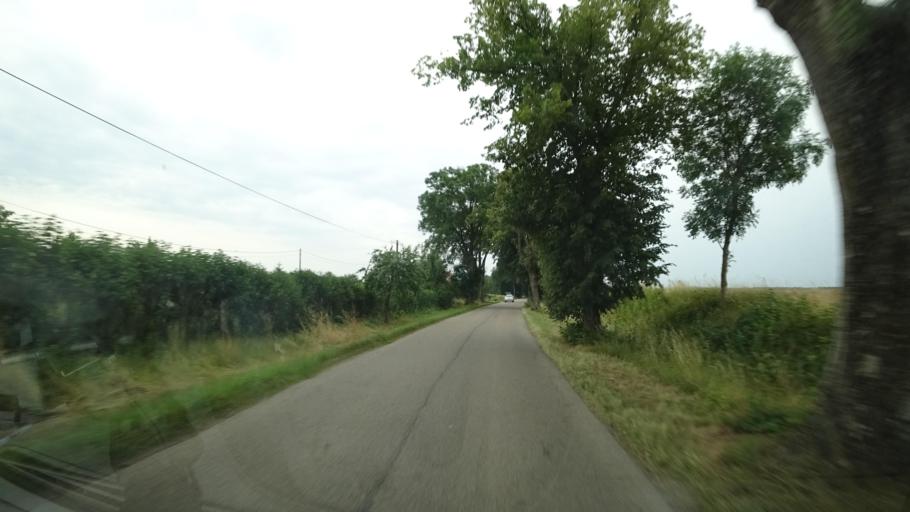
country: PL
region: Warmian-Masurian Voivodeship
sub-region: Powiat gizycki
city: Ryn
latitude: 53.9239
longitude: 21.5528
